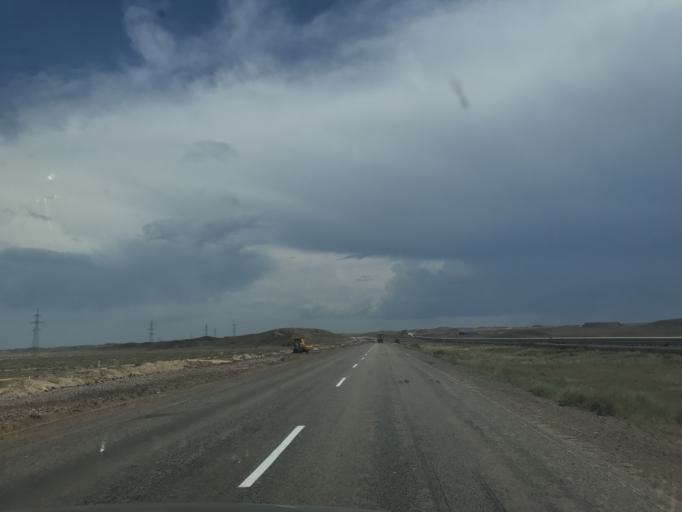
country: KZ
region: Zhambyl
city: Mynaral
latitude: 45.3788
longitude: 73.6536
